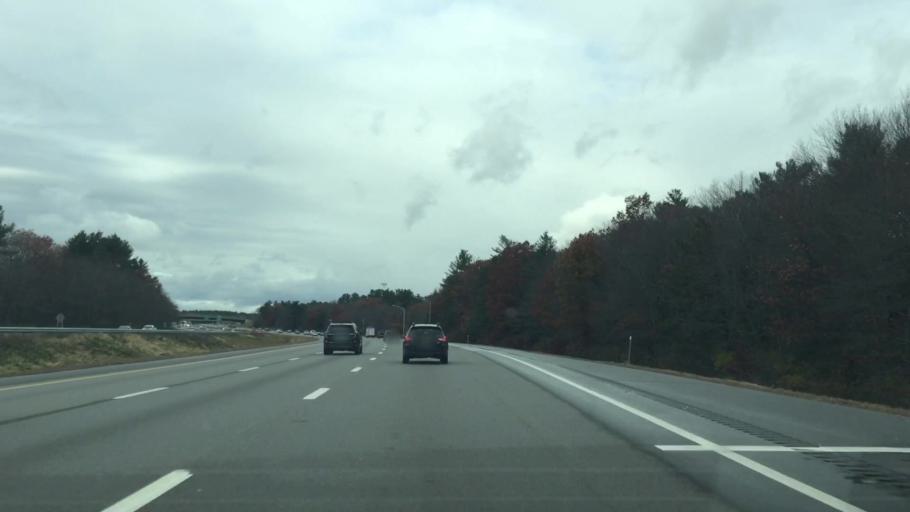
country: US
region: Massachusetts
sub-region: Essex County
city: Methuen
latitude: 42.7509
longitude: -71.2173
